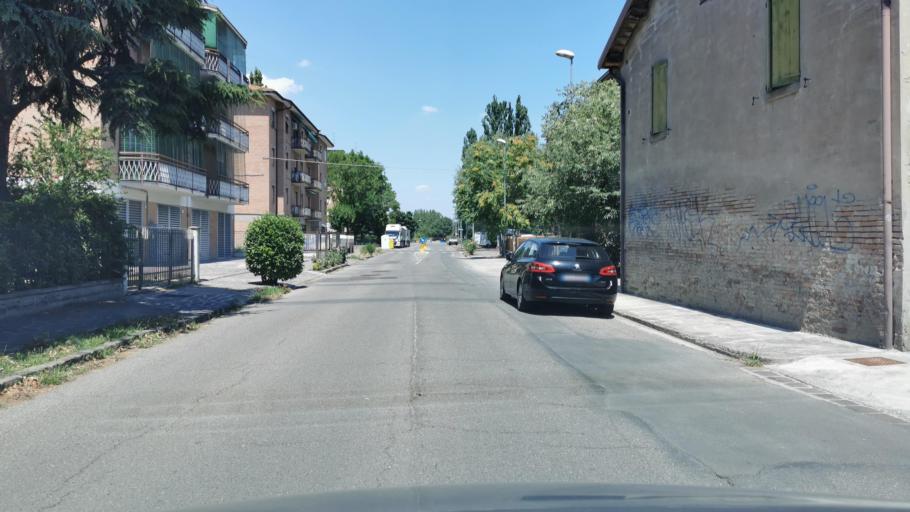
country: IT
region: Emilia-Romagna
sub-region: Provincia di Modena
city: Carpi Centro
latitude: 44.7922
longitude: 10.8877
